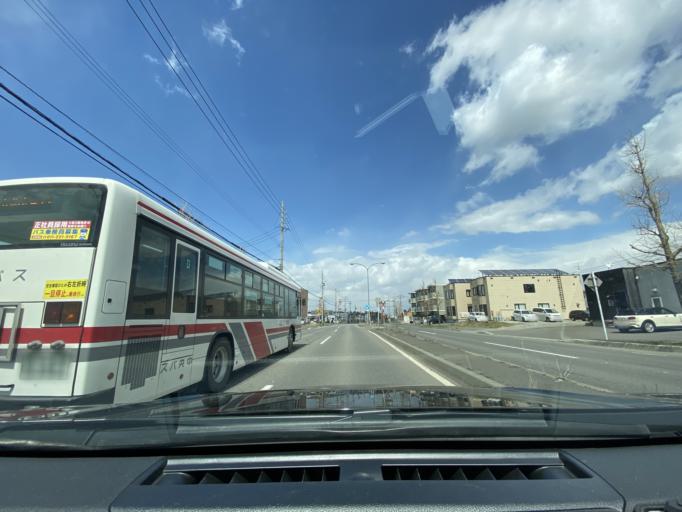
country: JP
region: Hokkaido
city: Kitahiroshima
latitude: 42.9816
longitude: 141.4837
